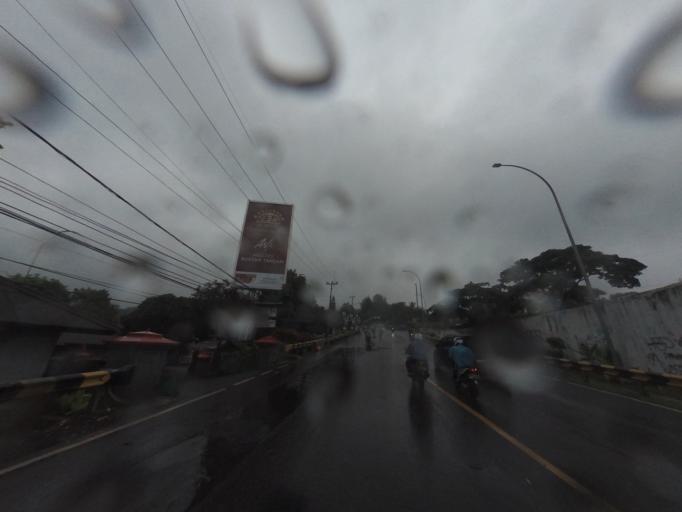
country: ID
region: West Java
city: Caringin
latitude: -6.6528
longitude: 106.8716
